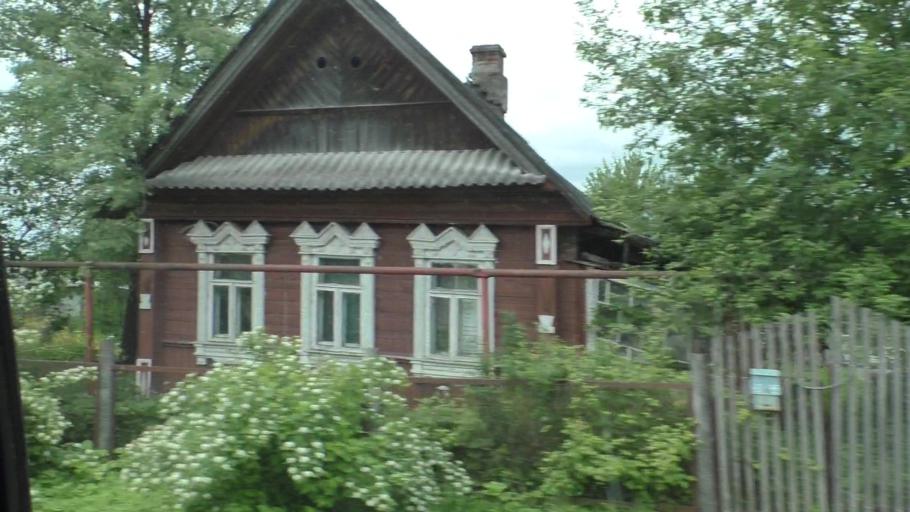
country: RU
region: Moskovskaya
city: Il'inskiy Pogost
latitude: 55.4710
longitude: 38.8956
